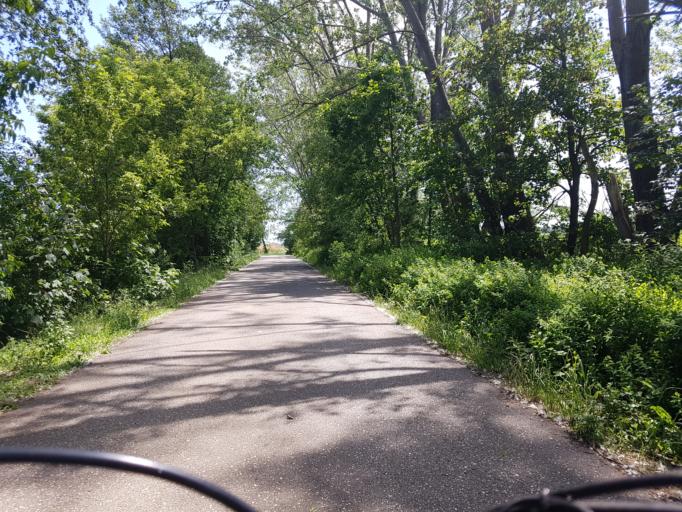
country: DE
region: Brandenburg
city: Bad Liebenwerda
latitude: 51.5410
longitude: 13.3652
